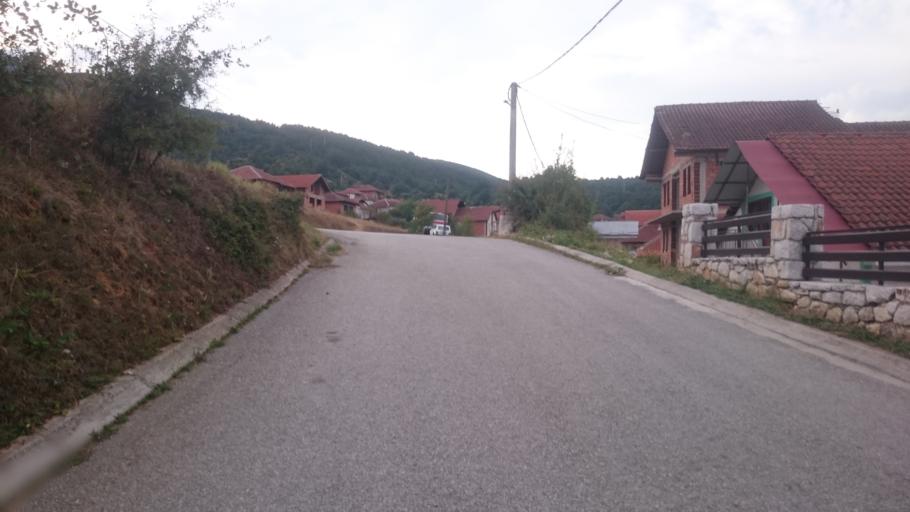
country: MK
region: Makedonski Brod
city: Makedonski Brod
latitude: 41.5174
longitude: 21.2155
